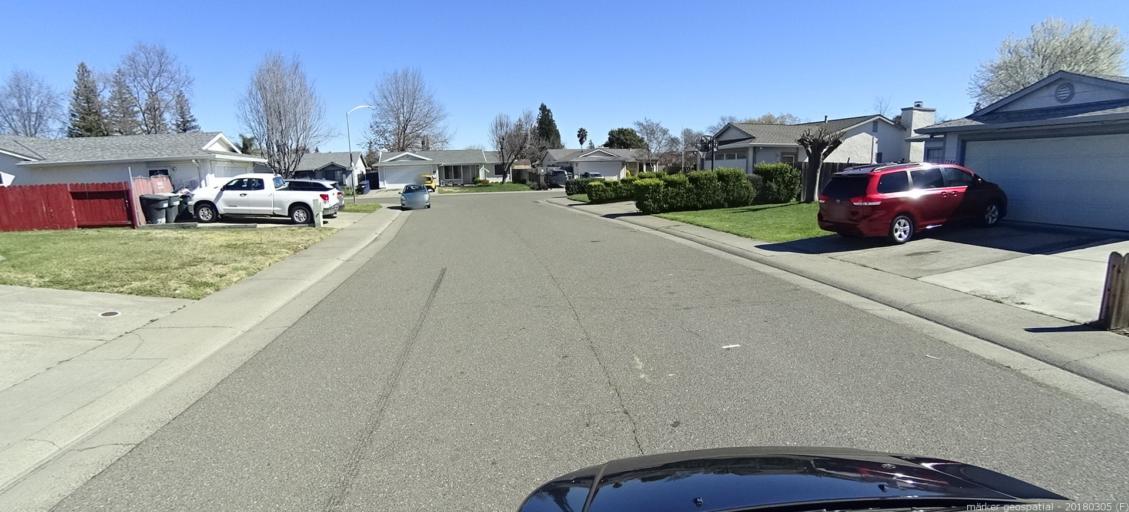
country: US
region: California
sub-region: Sacramento County
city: Florin
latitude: 38.4914
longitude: -121.3857
